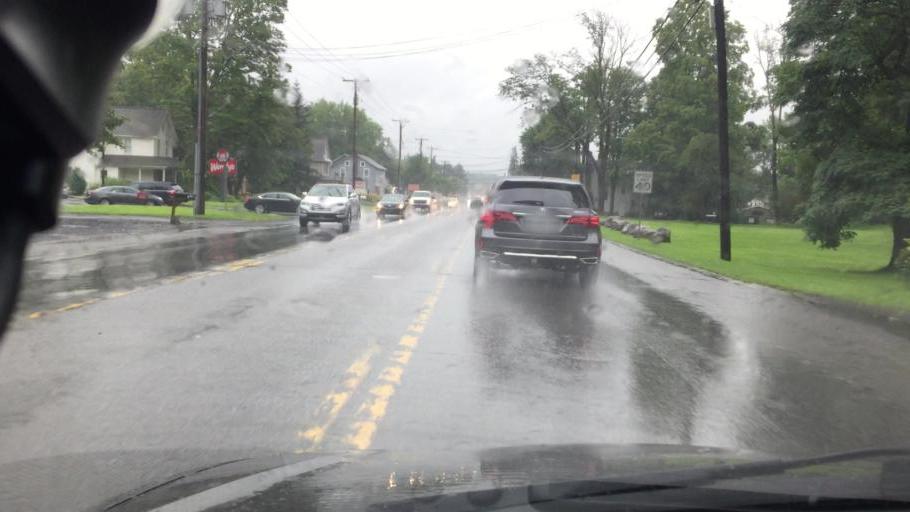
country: US
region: Pennsylvania
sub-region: Monroe County
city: Tannersville
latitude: 41.0435
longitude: -75.3083
